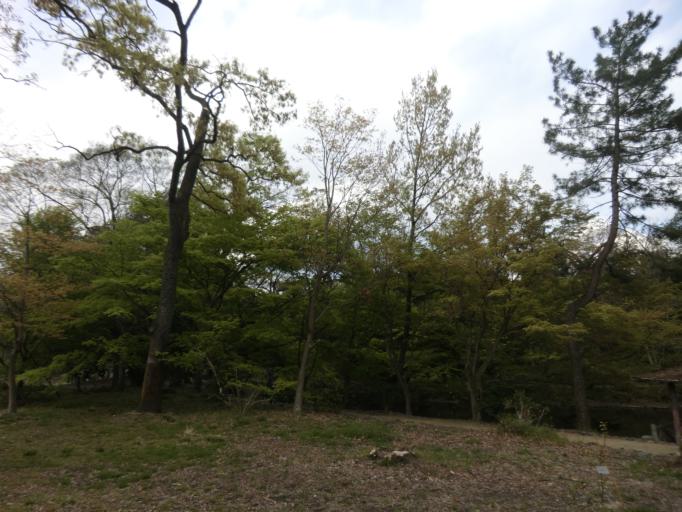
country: JP
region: Kyoto
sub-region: Kyoto-shi
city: Kamigyo-ku
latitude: 35.0497
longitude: 135.7609
